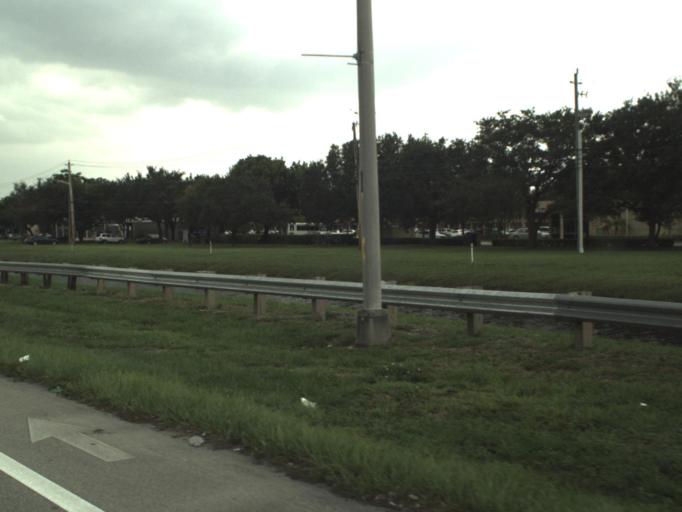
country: US
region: Florida
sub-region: Broward County
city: Sunshine Ranches
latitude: 26.0073
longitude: -80.3121
